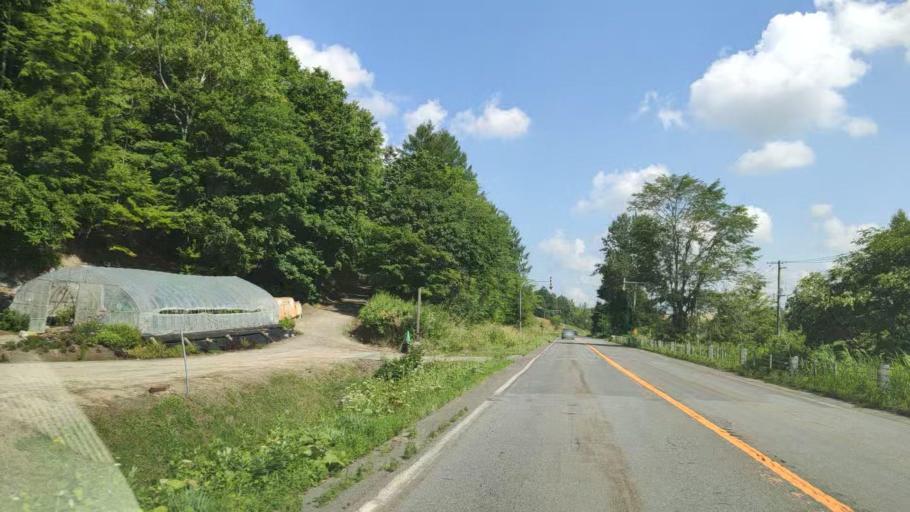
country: JP
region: Hokkaido
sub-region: Asahikawa-shi
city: Asahikawa
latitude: 43.5698
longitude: 142.4367
